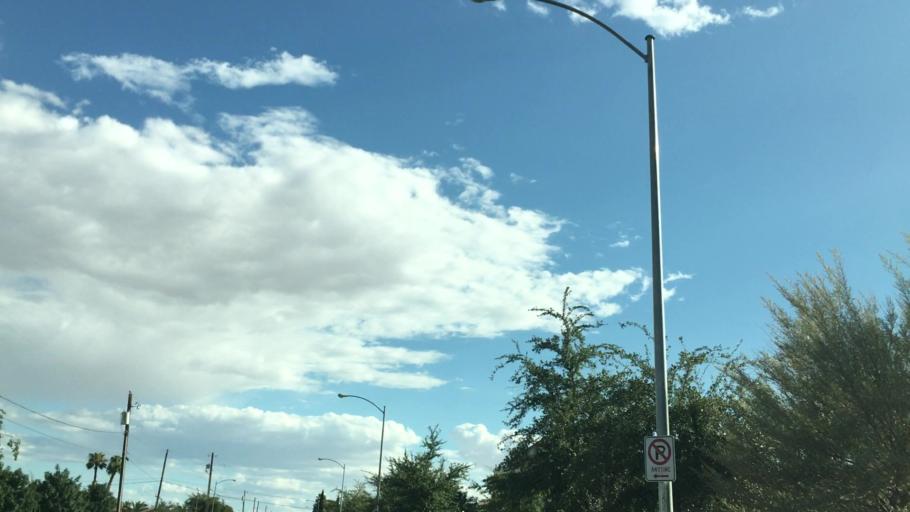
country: US
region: Nevada
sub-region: Clark County
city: Spring Valley
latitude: 36.1308
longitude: -115.2230
